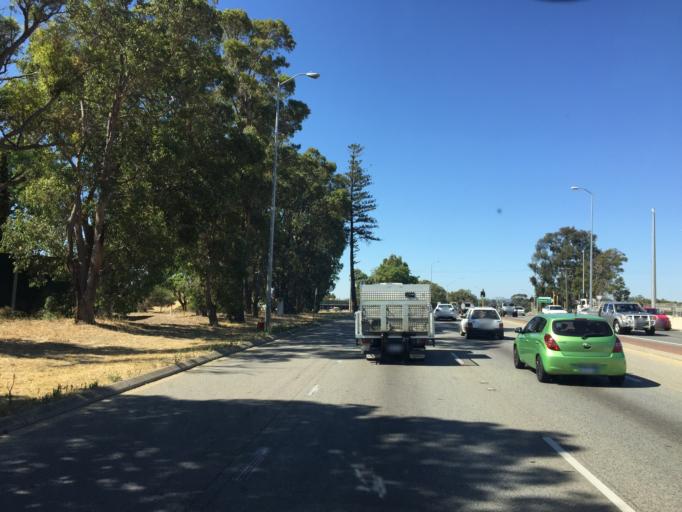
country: AU
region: Western Australia
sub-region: Kalamunda
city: Maida Vale
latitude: -31.9416
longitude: 116.0156
